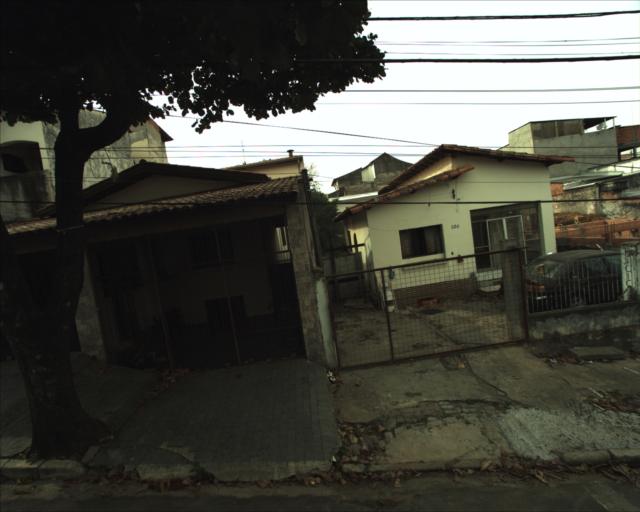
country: BR
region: Sao Paulo
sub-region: Sorocaba
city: Sorocaba
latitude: -23.4893
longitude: -47.4682
